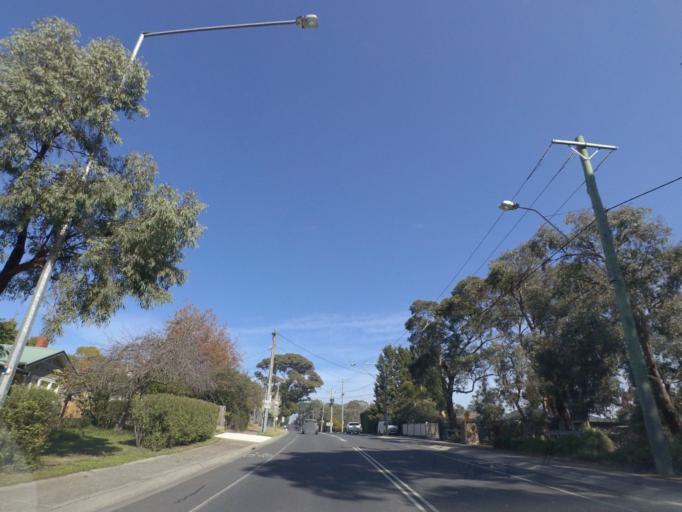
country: AU
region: Victoria
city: Mitcham
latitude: -37.8123
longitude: 145.2113
